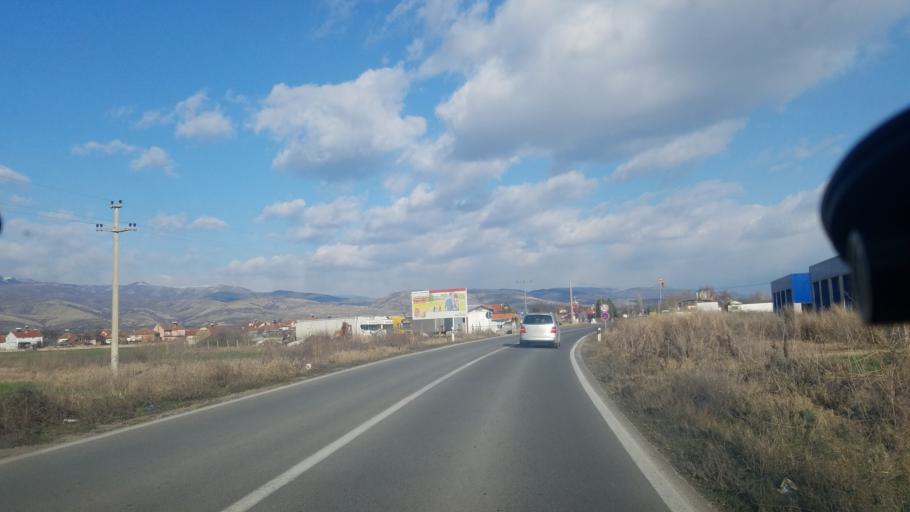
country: MK
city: Obleshevo
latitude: 41.8797
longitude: 22.3279
